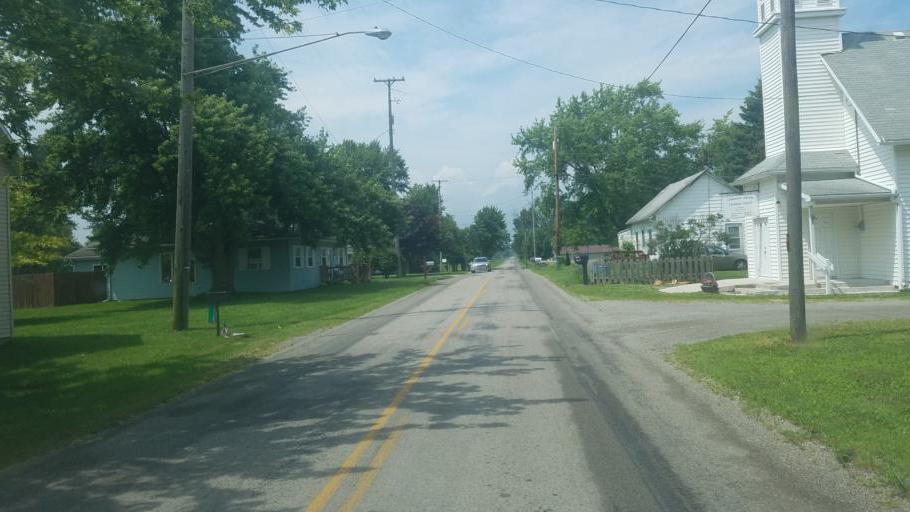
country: US
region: Ohio
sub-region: Union County
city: Richwood
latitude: 40.3885
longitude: -83.3491
